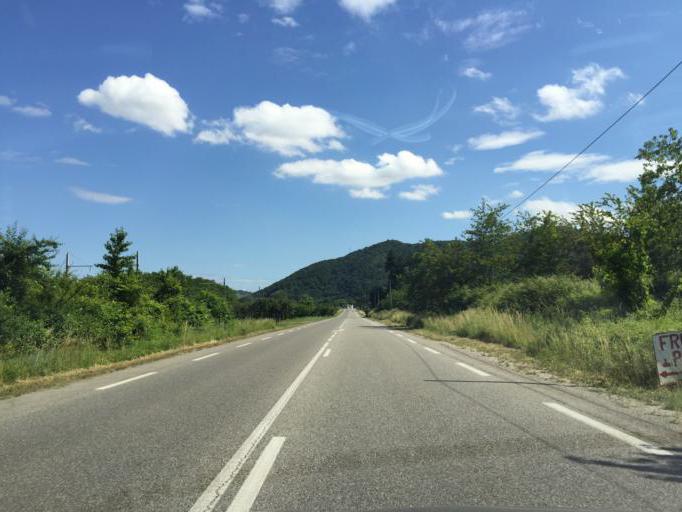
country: FR
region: Rhone-Alpes
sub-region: Departement de l'Ardeche
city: Saint-Jean-de-Muzols
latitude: 45.1201
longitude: 4.8014
